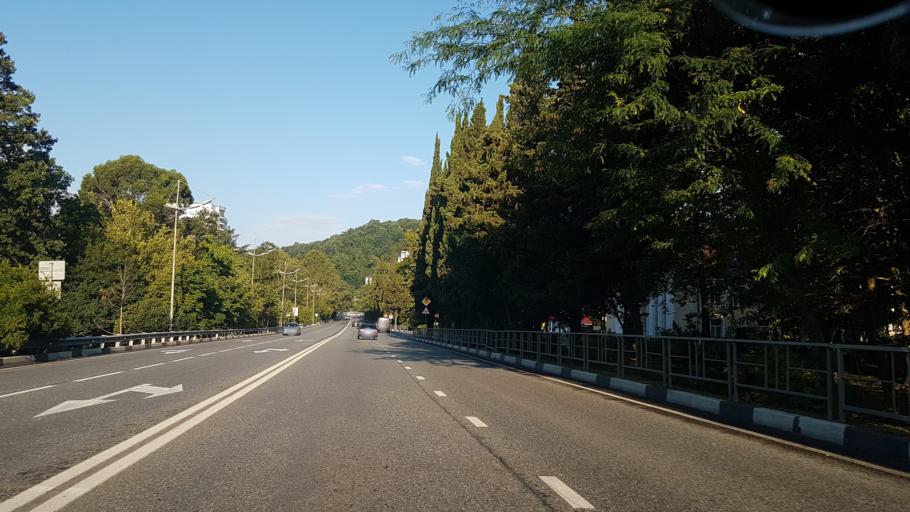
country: RU
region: Krasnodarskiy
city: Dagomys
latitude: 43.6601
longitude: 39.6579
